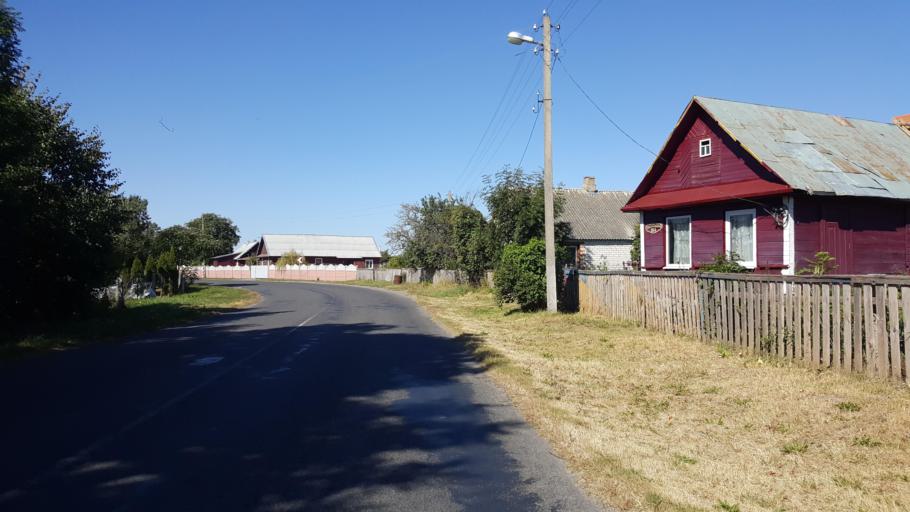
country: BY
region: Brest
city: Vysokaye
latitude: 52.2614
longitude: 23.5285
